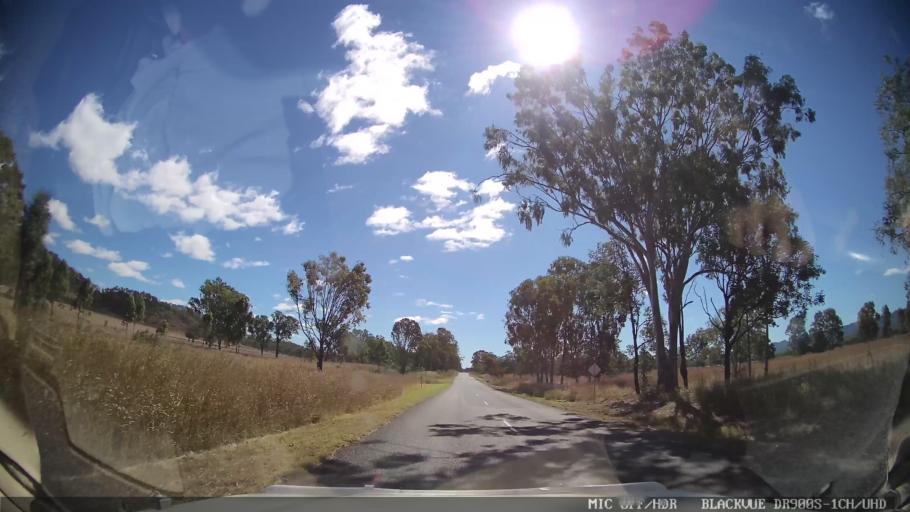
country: AU
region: Queensland
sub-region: Gladstone
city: Toolooa
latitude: -24.4476
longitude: 151.3437
